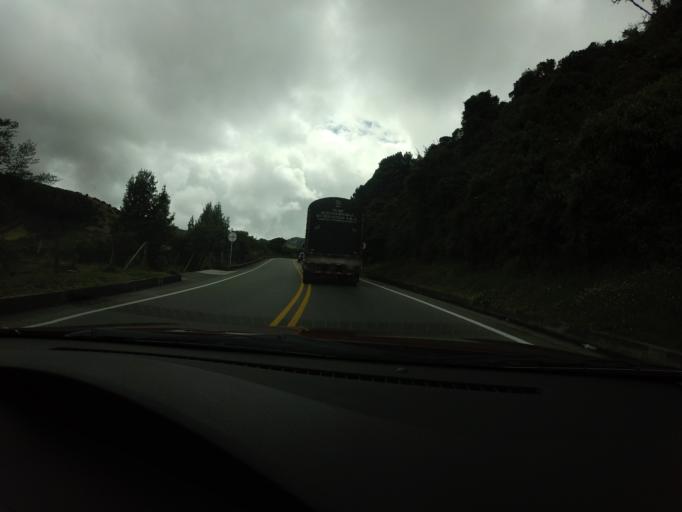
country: CO
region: Tolima
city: Herveo
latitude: 5.0576
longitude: -75.3178
